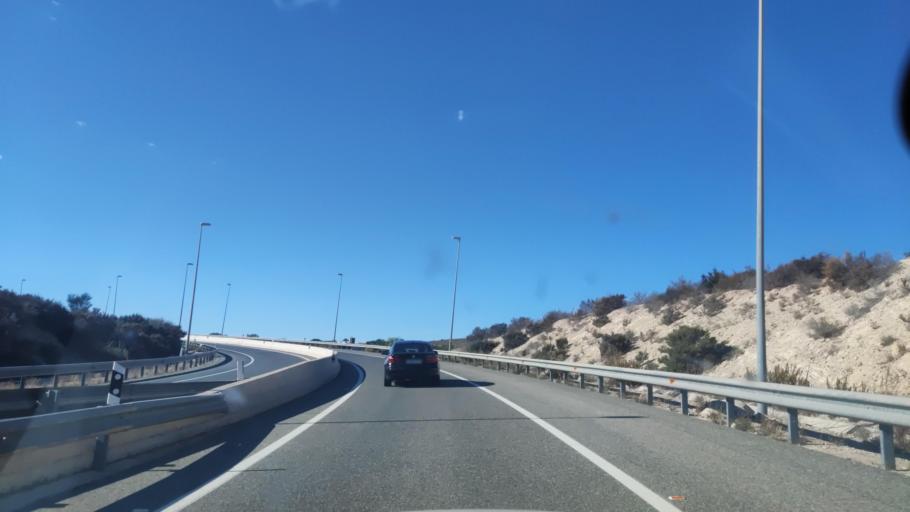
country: ES
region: Valencia
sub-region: Provincia de Alicante
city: el Campello
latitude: 38.4411
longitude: -0.4039
